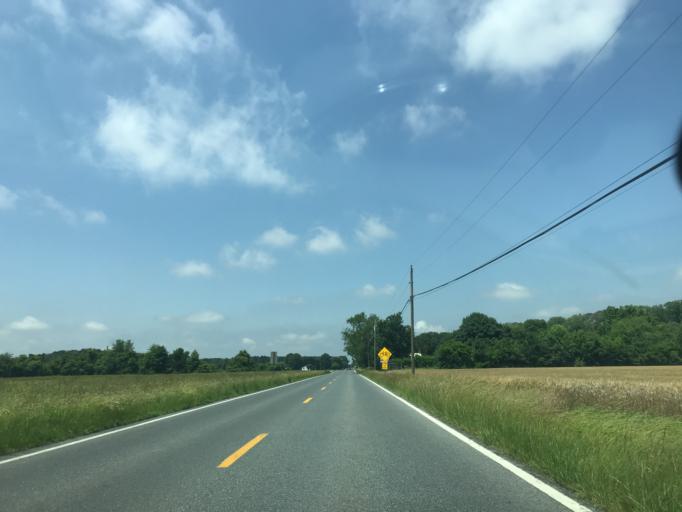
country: US
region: Maryland
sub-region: Dorchester County
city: Hurlock
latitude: 38.5942
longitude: -75.9515
